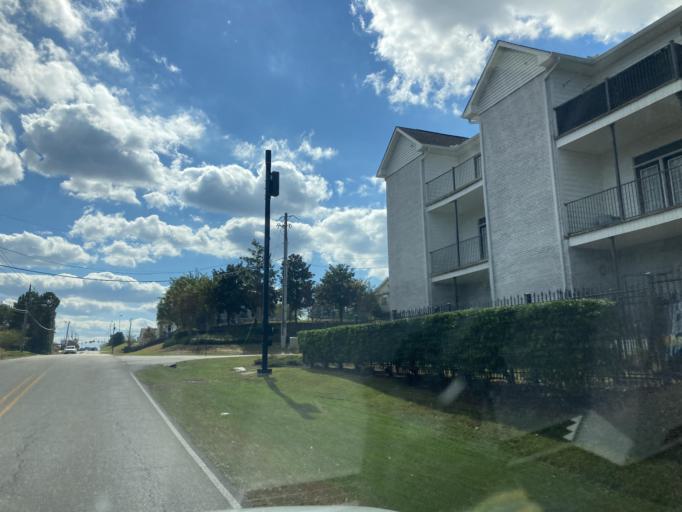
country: US
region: Mississippi
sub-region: Lamar County
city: Arnold Line
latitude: 31.3307
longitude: -89.3564
